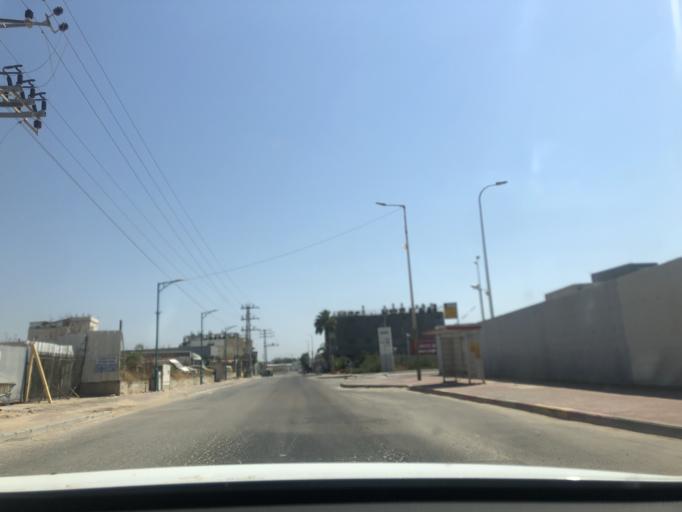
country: IL
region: Central District
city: Lod
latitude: 31.9676
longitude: 34.8924
